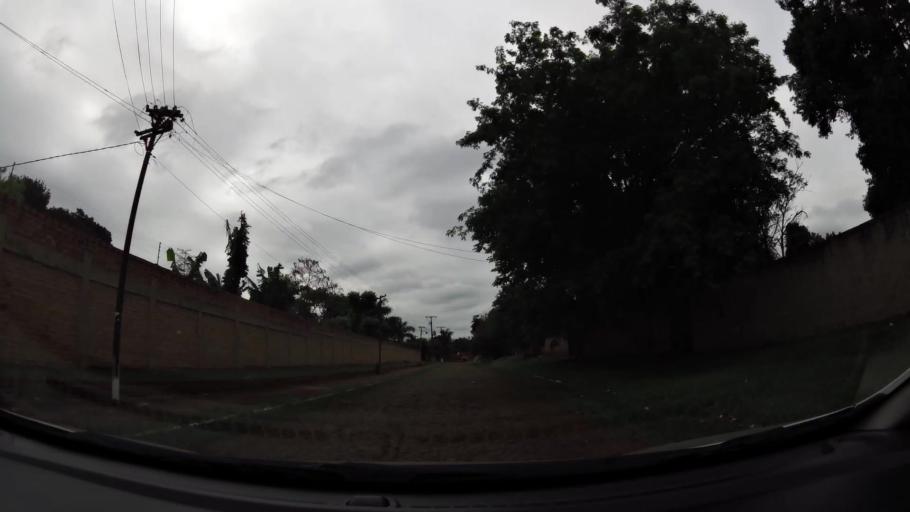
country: PY
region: Alto Parana
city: Ciudad del Este
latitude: -25.4116
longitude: -54.6365
